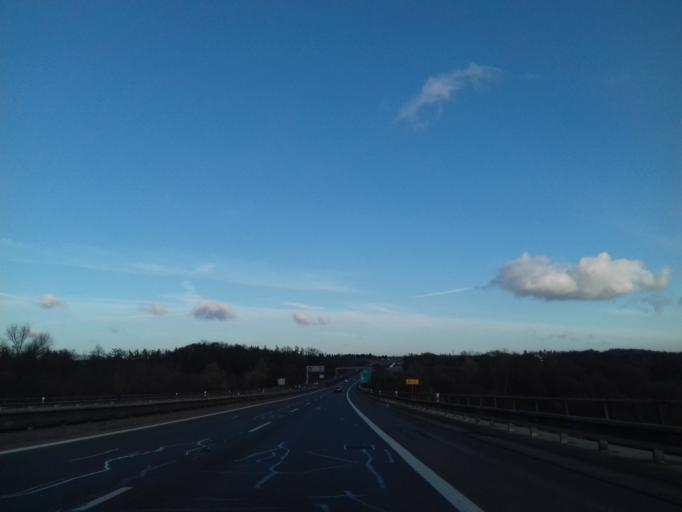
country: CZ
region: Plzensky
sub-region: Okres Rokycany
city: Rokycany
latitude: 49.7490
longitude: 13.5606
